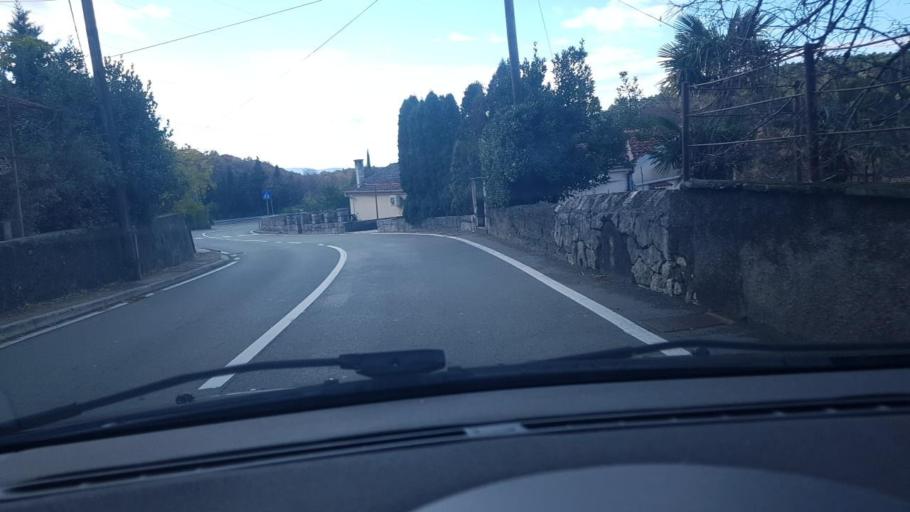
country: HR
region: Primorsko-Goranska
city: Cavle
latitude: 45.3408
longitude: 14.4653
